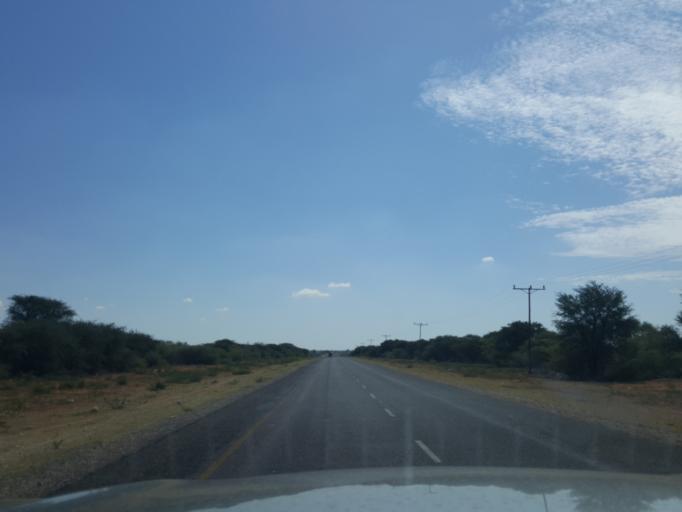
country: BW
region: Kweneng
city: Letlhakeng
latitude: -24.1198
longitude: 25.0681
